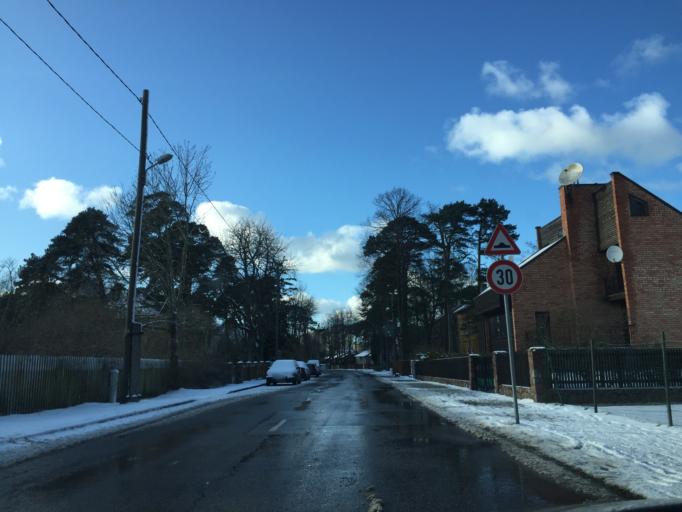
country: LV
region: Ventspils
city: Ventspils
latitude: 57.3875
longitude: 21.5413
